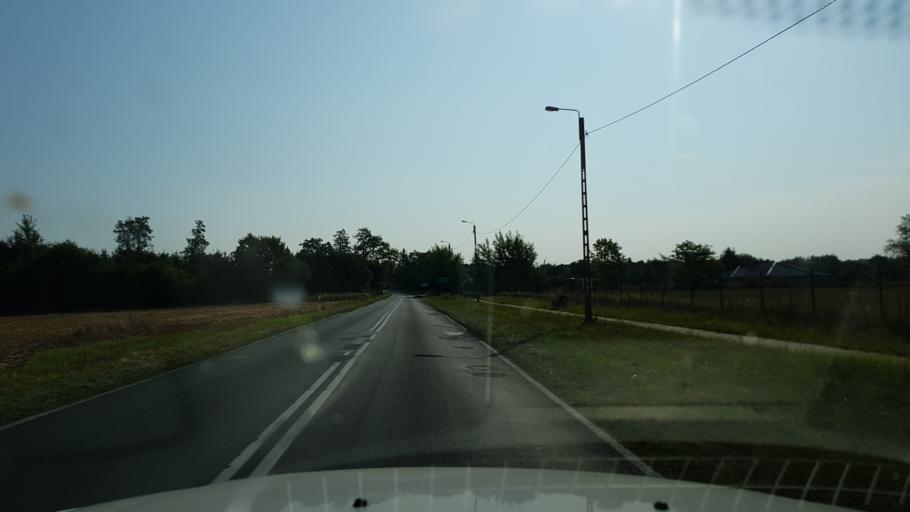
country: PL
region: West Pomeranian Voivodeship
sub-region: Powiat lobeski
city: Resko
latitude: 53.7751
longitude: 15.4252
